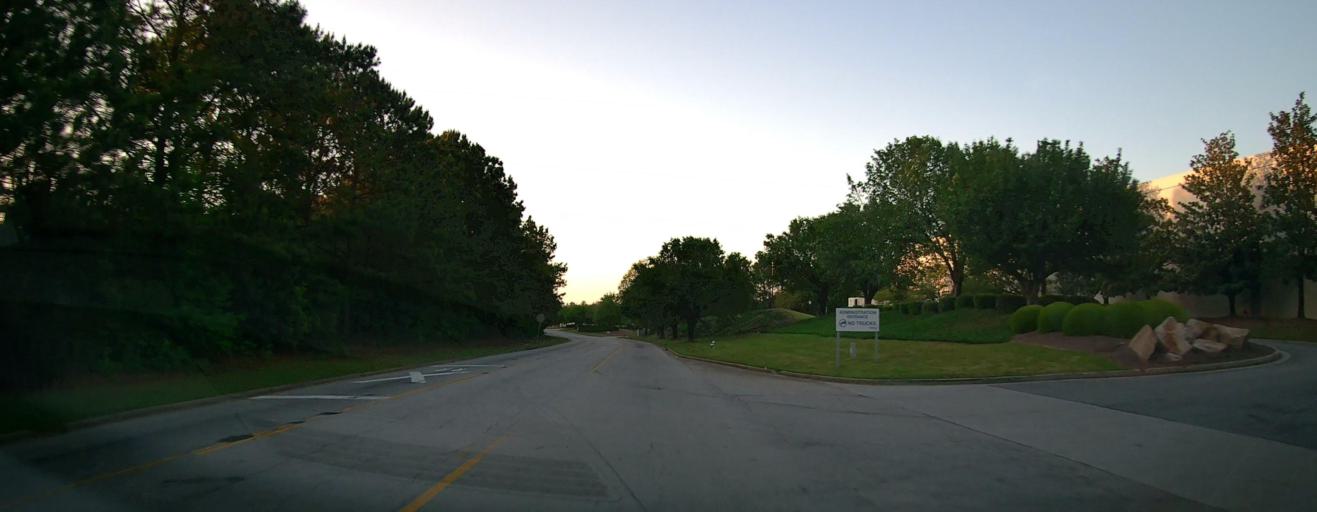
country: US
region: Georgia
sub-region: Henry County
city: McDonough
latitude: 33.4058
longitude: -84.1494
